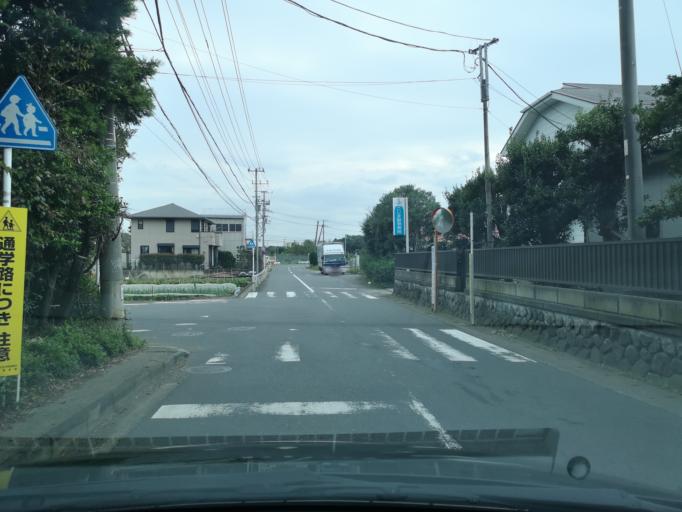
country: JP
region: Kanagawa
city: Chigasaki
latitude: 35.3846
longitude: 139.3984
